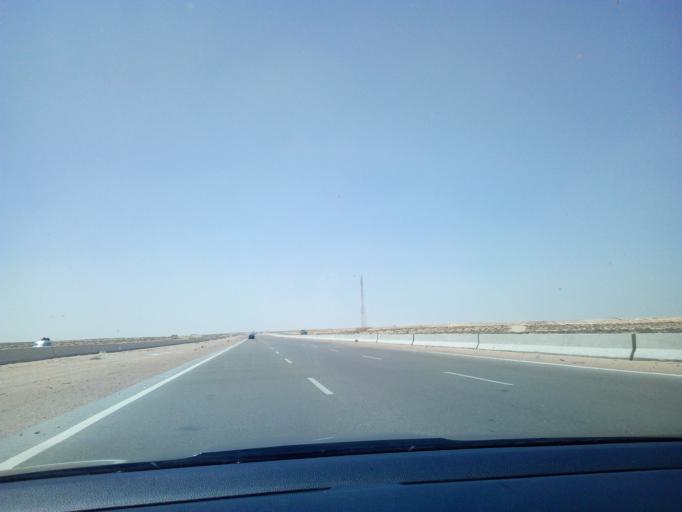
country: EG
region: Al Buhayrah
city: Abu al Matamir
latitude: 30.6330
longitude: 29.7596
